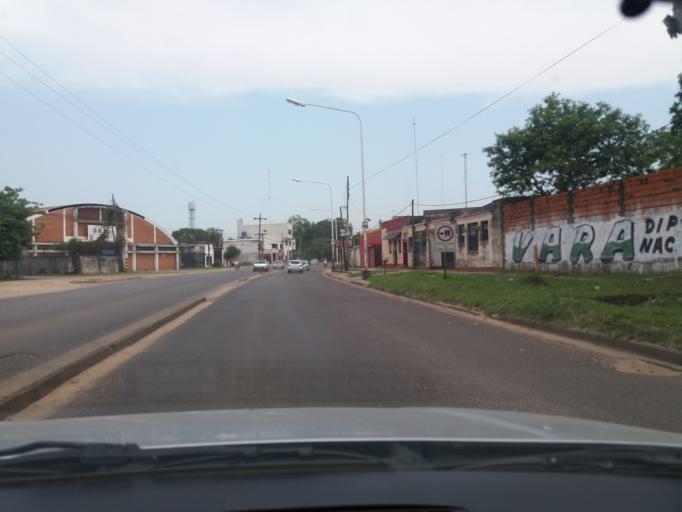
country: AR
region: Corrientes
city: Corrientes
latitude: -27.5125
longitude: -58.8086
